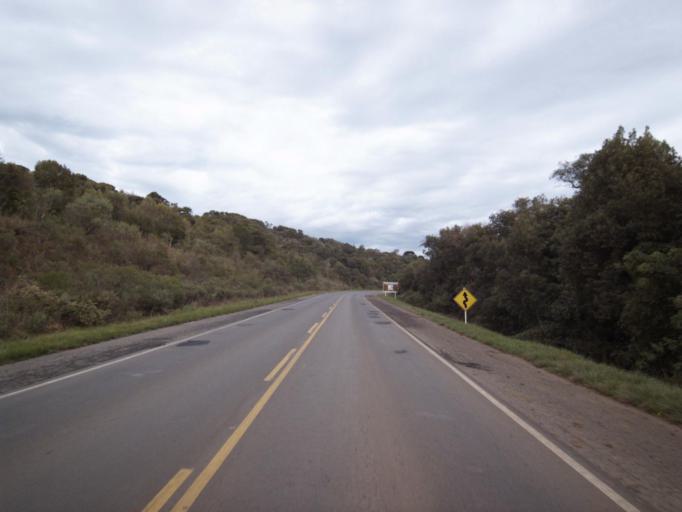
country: BR
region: Santa Catarina
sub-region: Concordia
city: Concordia
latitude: -26.9653
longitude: -51.8429
